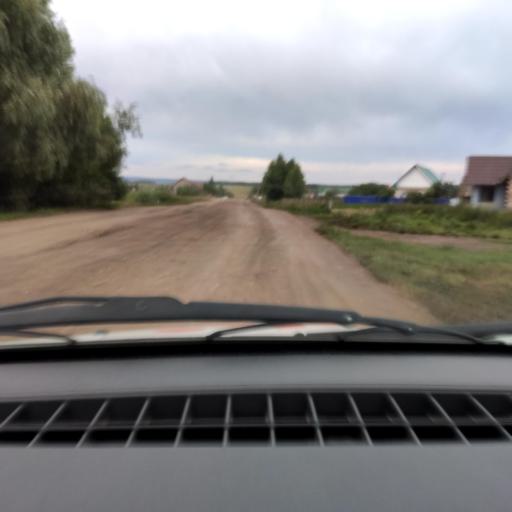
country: RU
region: Bashkortostan
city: Avdon
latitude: 54.5096
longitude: 55.7760
